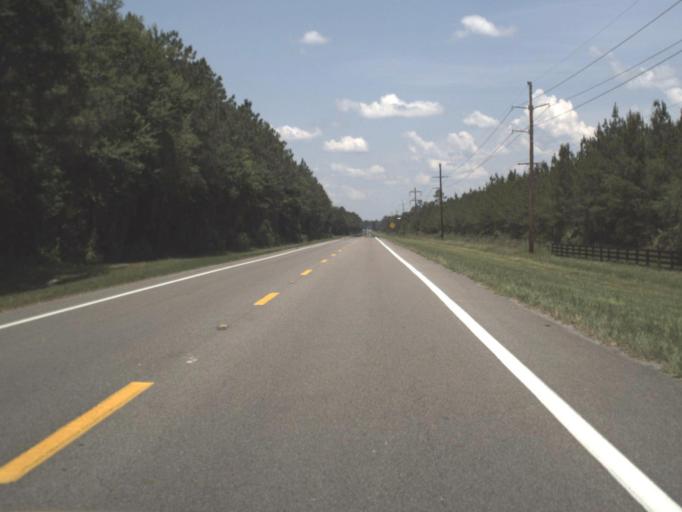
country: US
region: Florida
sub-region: Union County
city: Lake Butler
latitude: 30.0105
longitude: -82.2992
